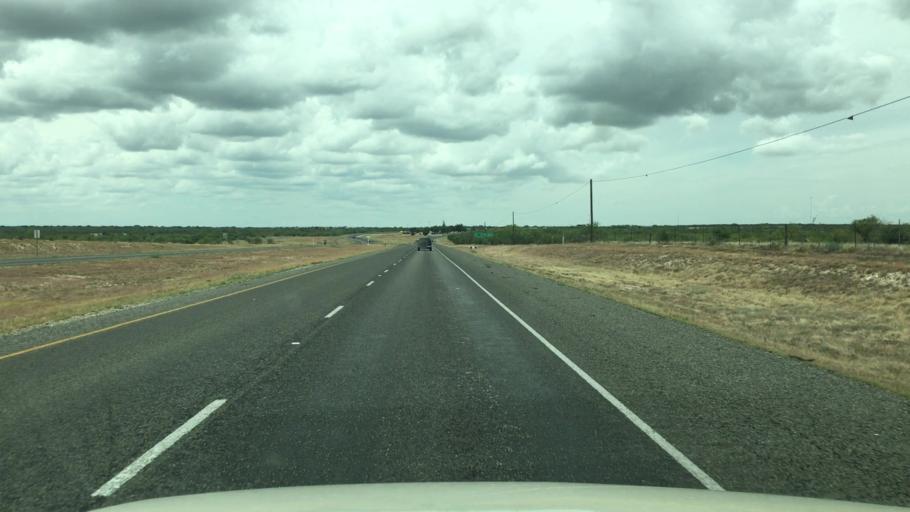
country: US
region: Texas
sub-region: Concho County
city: Eden
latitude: 31.2175
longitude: -99.9505
